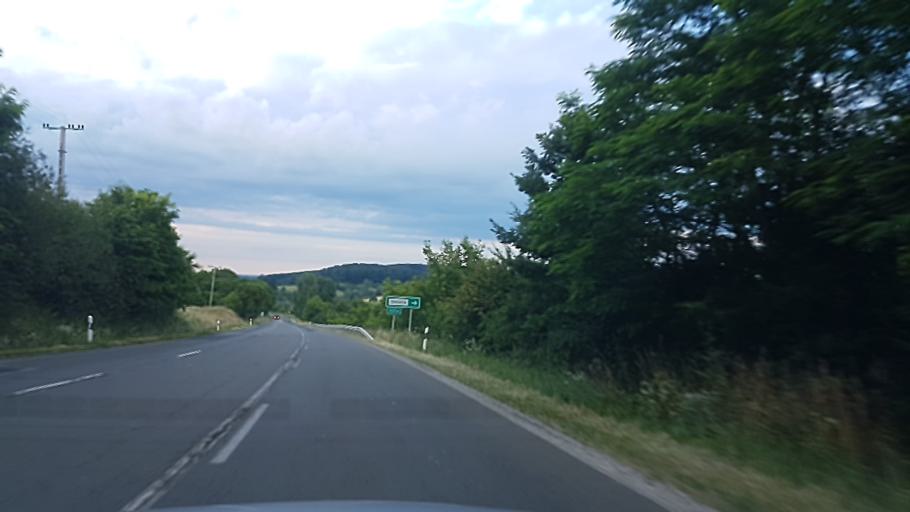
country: HU
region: Somogy
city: Kaposvar
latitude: 46.2777
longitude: 17.8214
